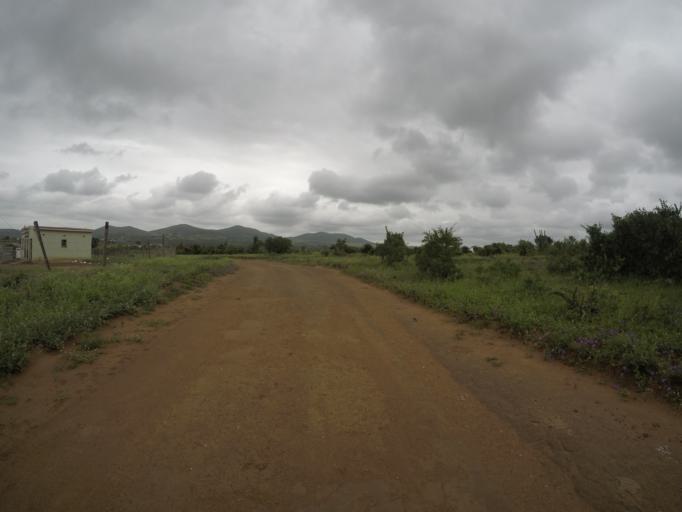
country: ZA
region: KwaZulu-Natal
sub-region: uThungulu District Municipality
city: Empangeni
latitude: -28.6030
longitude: 31.8641
